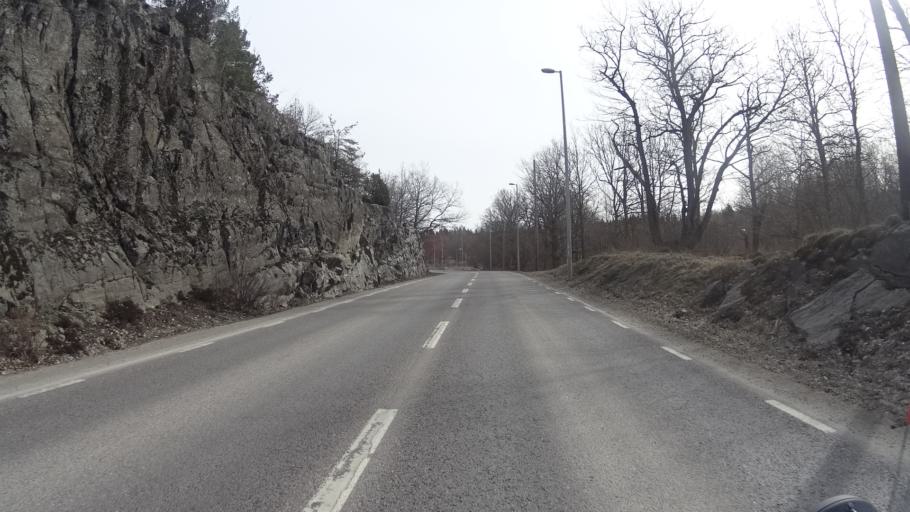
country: SE
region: Stockholm
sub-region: Nacka Kommun
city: Nacka
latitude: 59.2896
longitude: 18.1570
